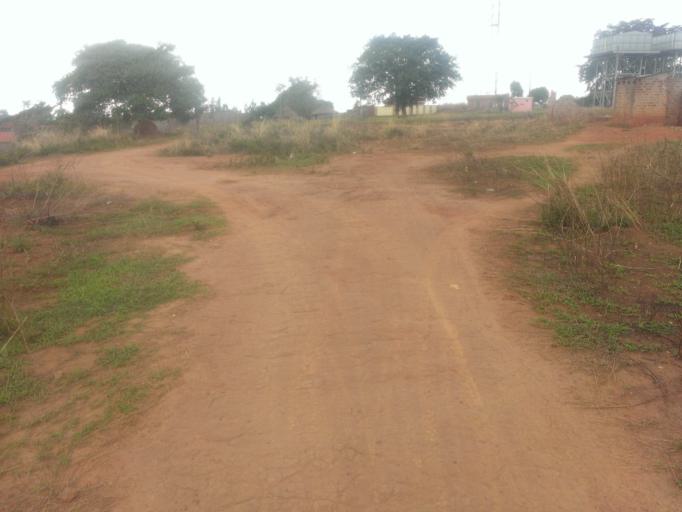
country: UG
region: Northern Region
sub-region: Gulu District
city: Gulu
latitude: 2.7812
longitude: 32.2959
